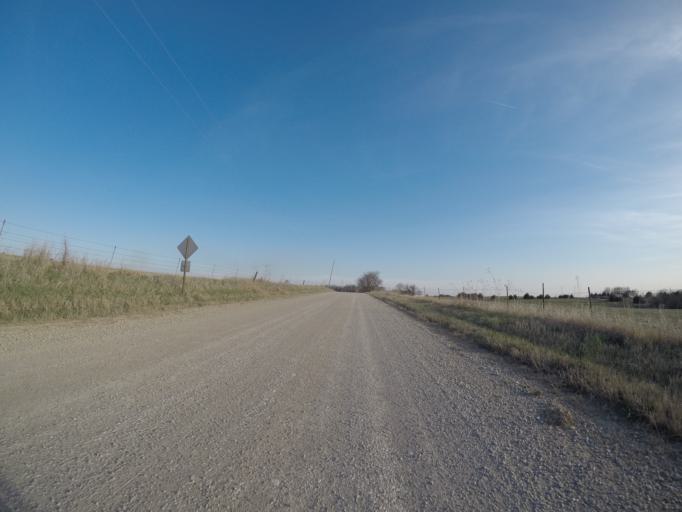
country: US
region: Kansas
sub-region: Riley County
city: Manhattan
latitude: 39.2455
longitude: -96.6912
